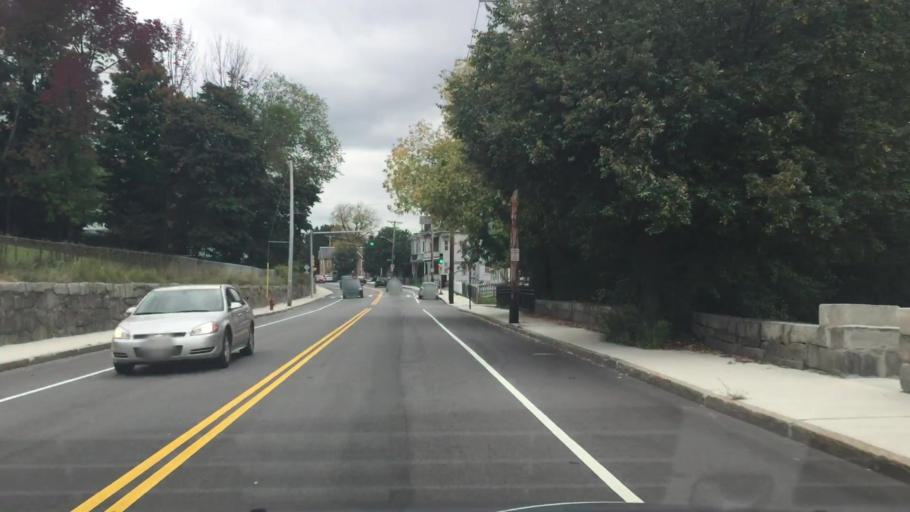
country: US
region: Massachusetts
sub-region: Middlesex County
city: Dracut
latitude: 42.6591
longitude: -71.3036
